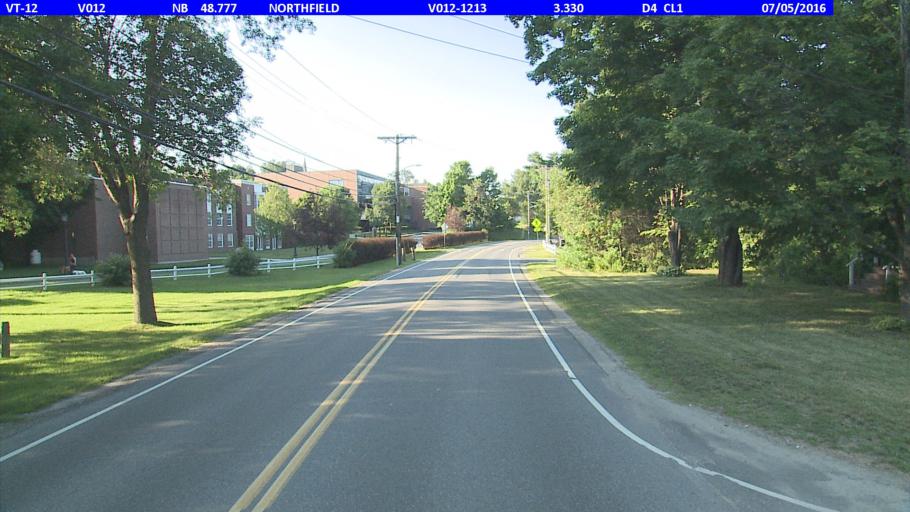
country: US
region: Vermont
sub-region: Washington County
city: Northfield
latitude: 44.1368
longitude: -72.6591
